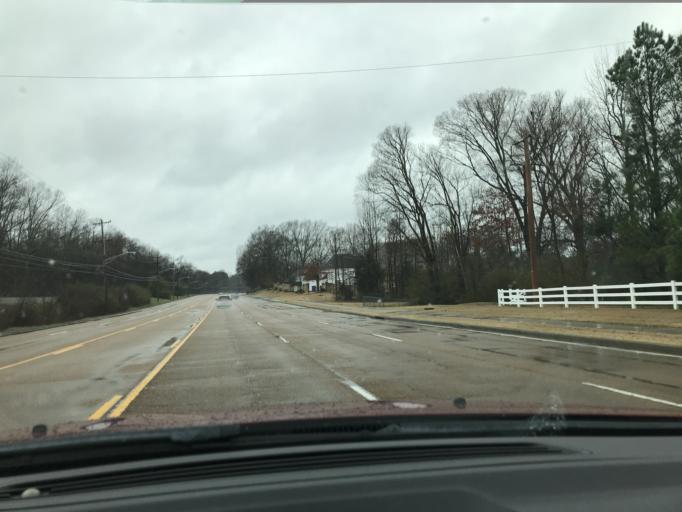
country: US
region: Tennessee
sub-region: Shelby County
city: Collierville
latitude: 35.0478
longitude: -89.7167
